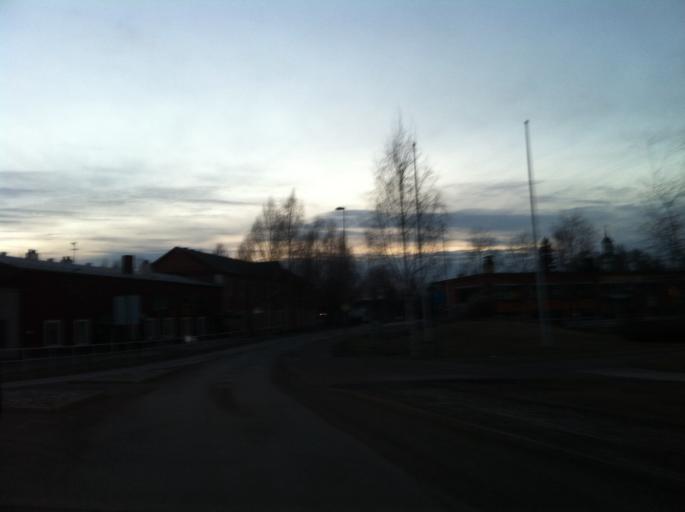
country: SE
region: Dalarna
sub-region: Orsa Kommun
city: Orsa
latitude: 61.1174
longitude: 14.6201
